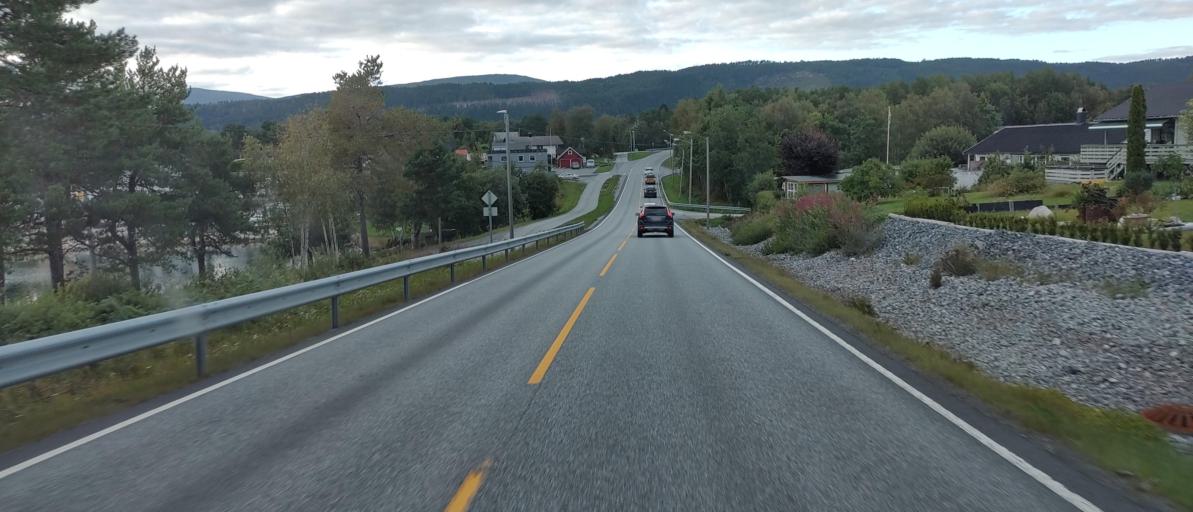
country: NO
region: More og Romsdal
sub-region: Molde
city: Hjelset
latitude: 62.7160
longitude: 7.4279
